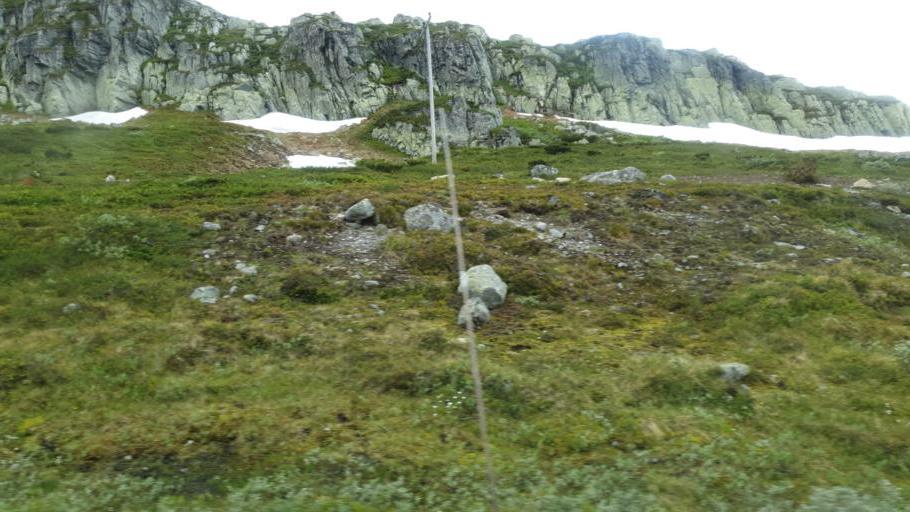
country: NO
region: Oppland
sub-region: Vestre Slidre
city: Slidre
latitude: 61.3104
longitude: 8.8071
